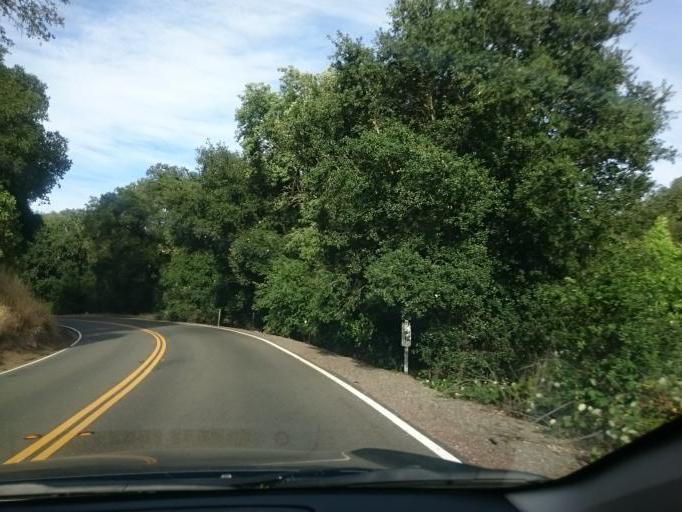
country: US
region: California
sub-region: Napa County
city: Yountville
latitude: 38.5053
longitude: -122.2786
